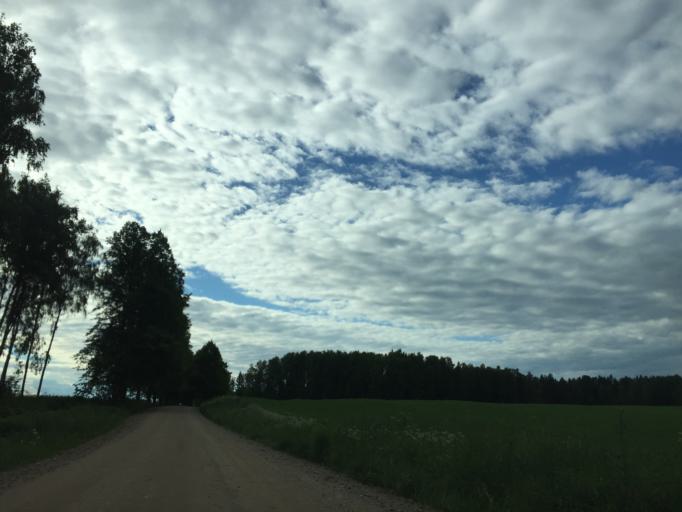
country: LV
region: Amatas Novads
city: Drabesi
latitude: 57.2533
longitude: 25.1714
